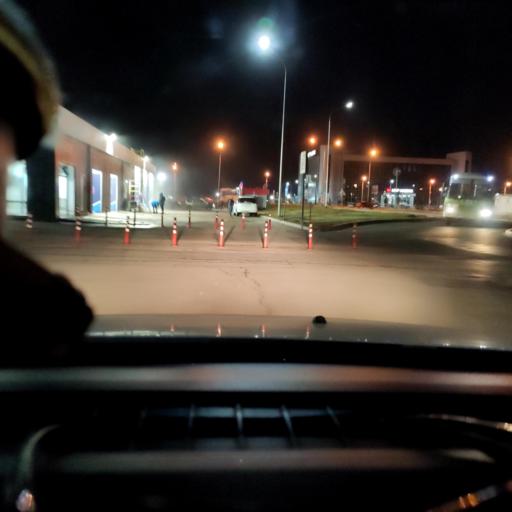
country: RU
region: Samara
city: Samara
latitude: 53.1368
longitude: 50.1733
